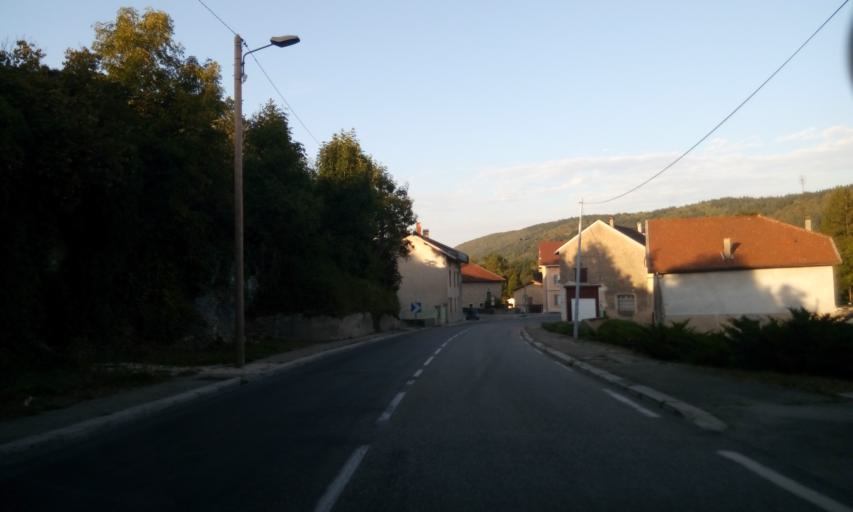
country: FR
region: Rhone-Alpes
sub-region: Departement de l'Ain
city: Saint-Martin-du-Frene
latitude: 46.1282
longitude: 5.5377
